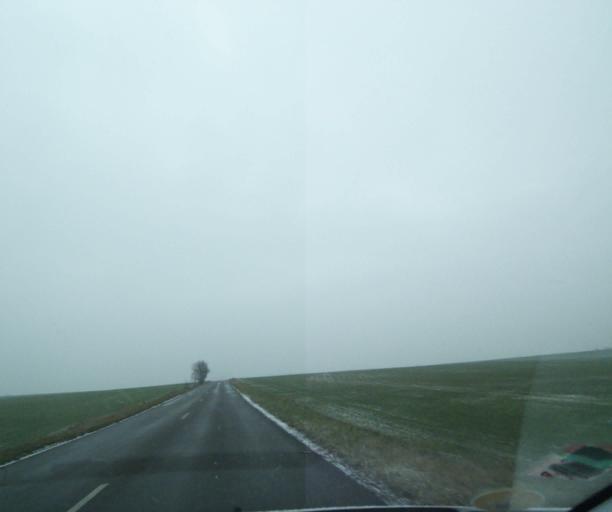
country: FR
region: Champagne-Ardenne
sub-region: Departement de la Haute-Marne
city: Wassy
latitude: 48.4841
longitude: 4.9892
